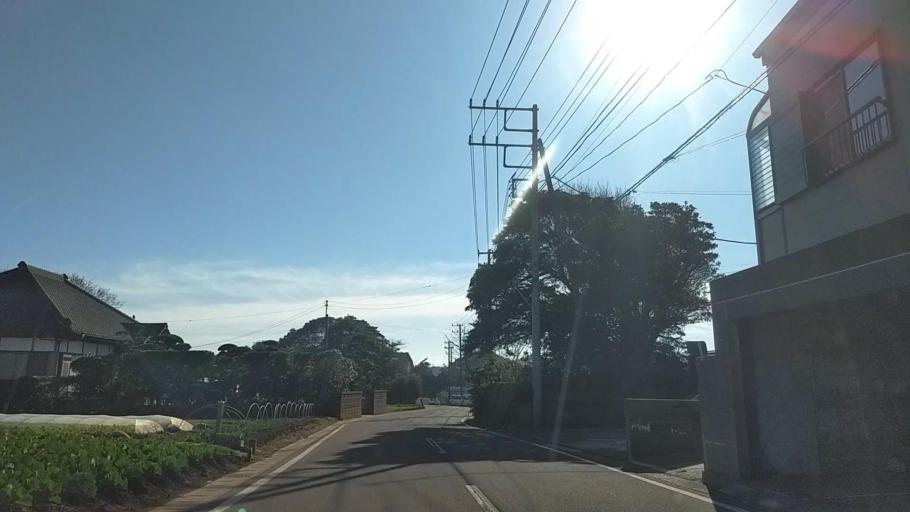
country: JP
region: Chiba
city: Hasaki
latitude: 35.7180
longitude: 140.8463
